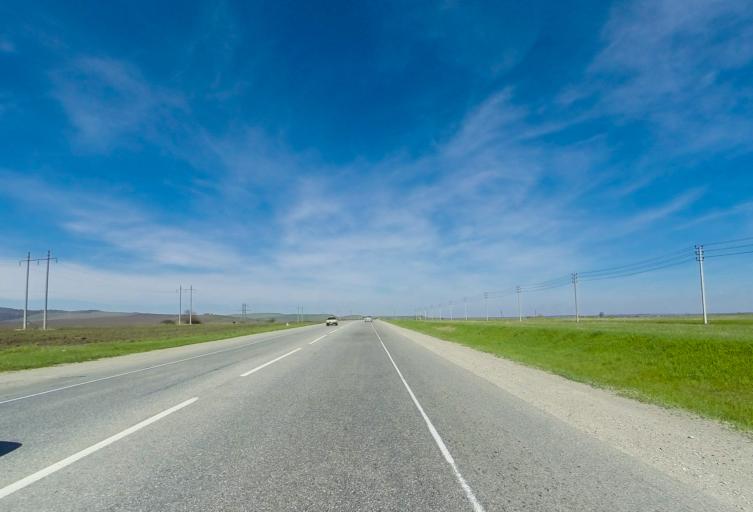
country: RU
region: Kabardino-Balkariya
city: Dugulubgey
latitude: 43.6506
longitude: 43.5155
